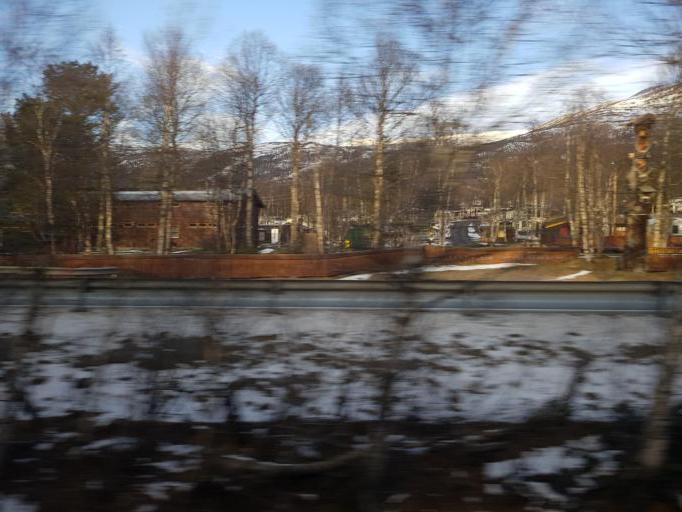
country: NO
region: Sor-Trondelag
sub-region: Oppdal
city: Oppdal
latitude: 62.6098
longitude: 9.7352
